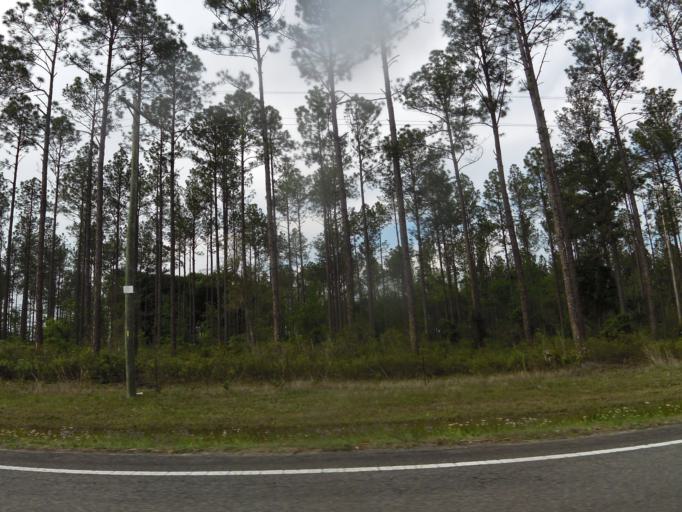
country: US
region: Florida
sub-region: Nassau County
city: Hilliard
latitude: 30.6973
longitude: -81.7908
